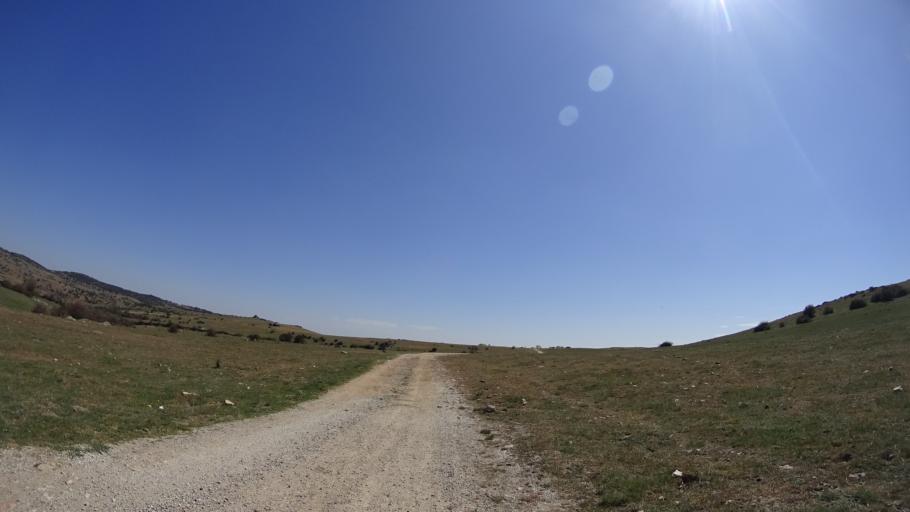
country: ES
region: Madrid
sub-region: Provincia de Madrid
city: Colmenar Viejo
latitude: 40.6936
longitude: -3.7575
